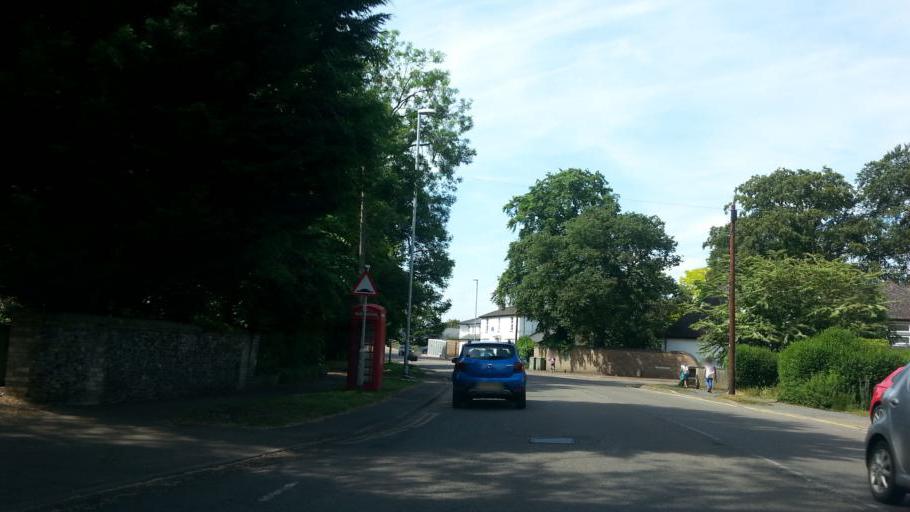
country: GB
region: England
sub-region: Cambridgeshire
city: Sawston
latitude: 52.1512
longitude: 0.1359
